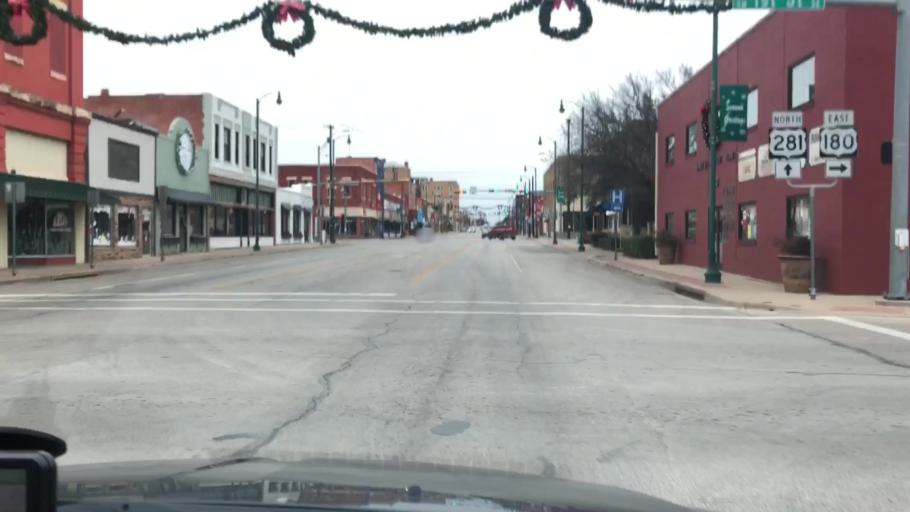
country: US
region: Texas
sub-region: Palo Pinto County
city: Mineral Wells
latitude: 32.8085
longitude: -98.1129
